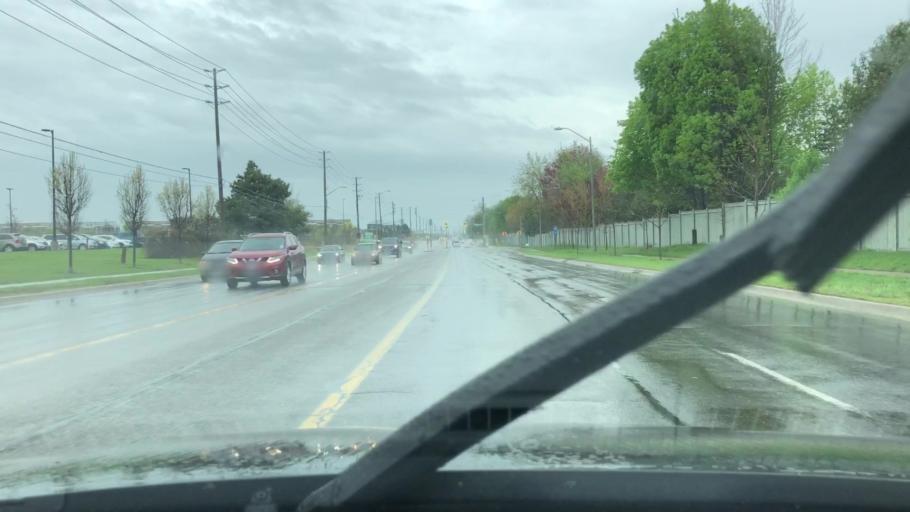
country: CA
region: Ontario
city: Markham
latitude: 43.8823
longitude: -79.2357
